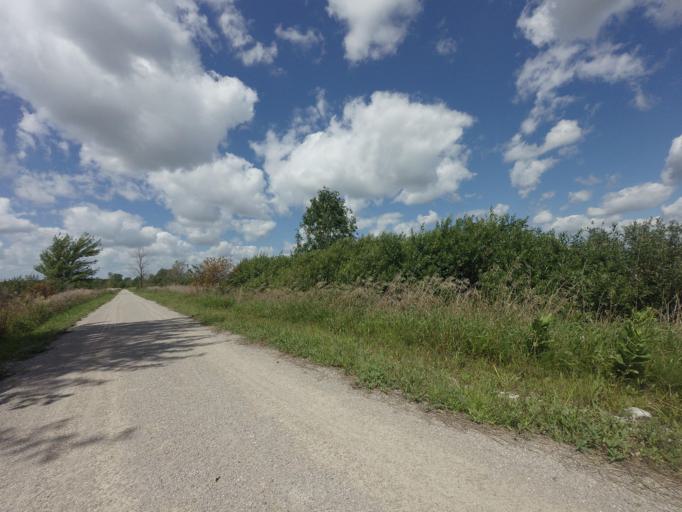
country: CA
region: Ontario
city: North Perth
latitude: 43.5832
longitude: -81.0650
